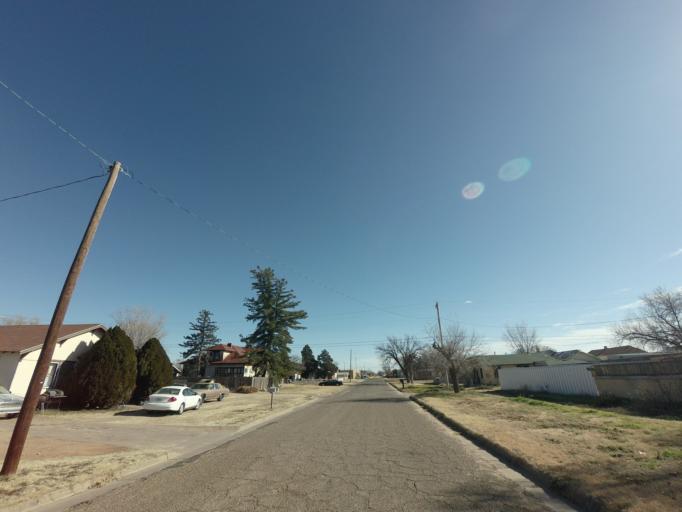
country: US
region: New Mexico
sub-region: Curry County
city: Clovis
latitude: 34.4057
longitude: -103.2090
